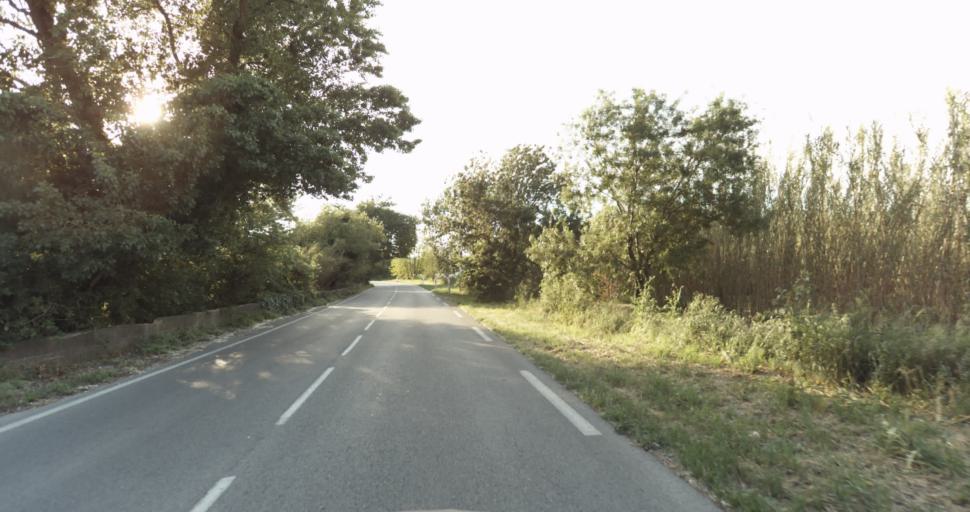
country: FR
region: Provence-Alpes-Cote d'Azur
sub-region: Departement du Var
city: Hyeres
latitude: 43.1334
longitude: 6.1620
